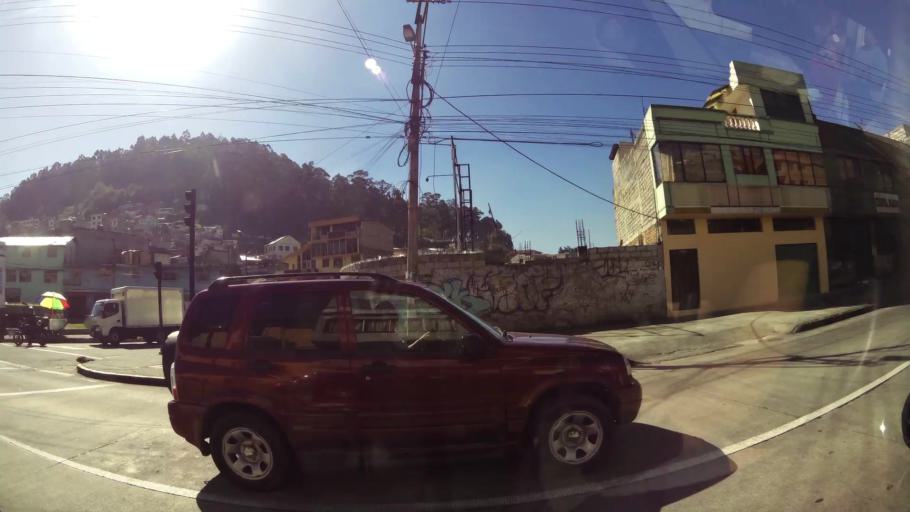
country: EC
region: Pichincha
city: Quito
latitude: -0.2331
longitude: -78.5245
